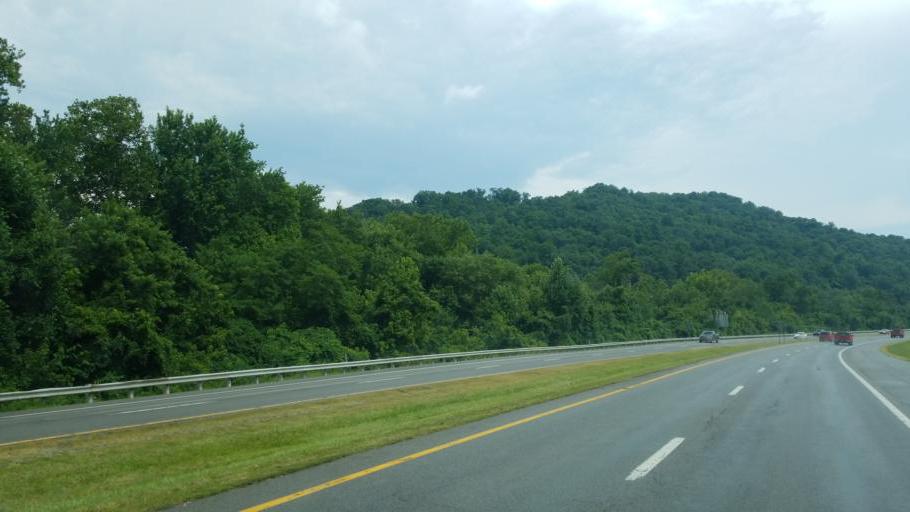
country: US
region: West Virginia
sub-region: Logan County
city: Chapmanville
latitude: 37.9572
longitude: -82.0174
